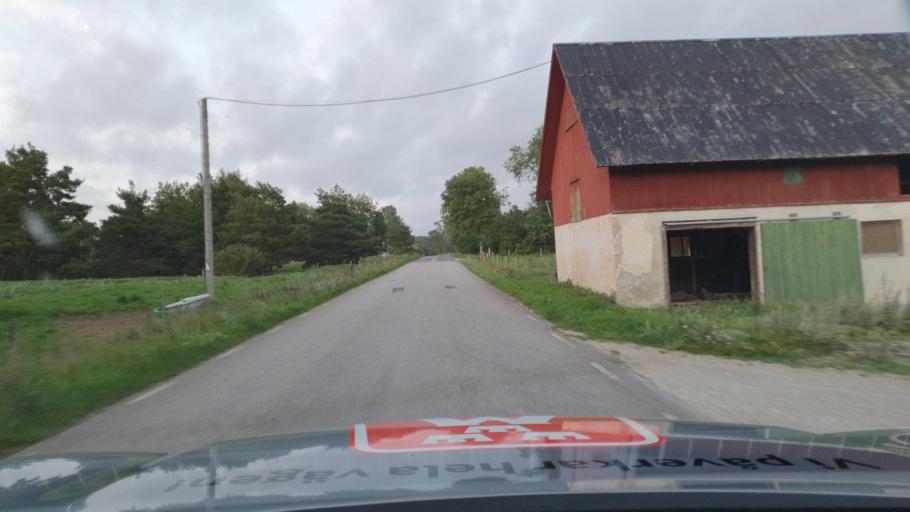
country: SE
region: Gotland
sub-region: Gotland
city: Klintehamn
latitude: 57.2886
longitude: 18.2127
